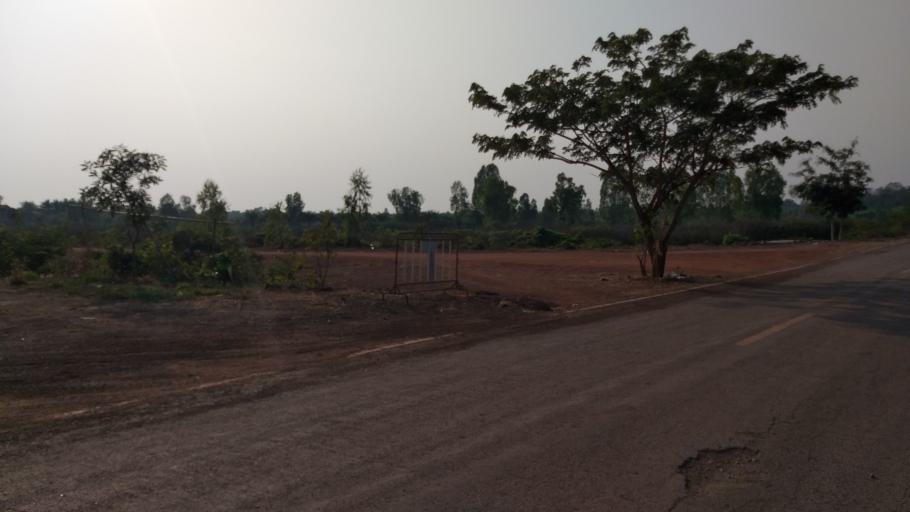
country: TH
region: Changwat Udon Thani
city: Ban Dung
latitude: 17.7428
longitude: 103.3565
